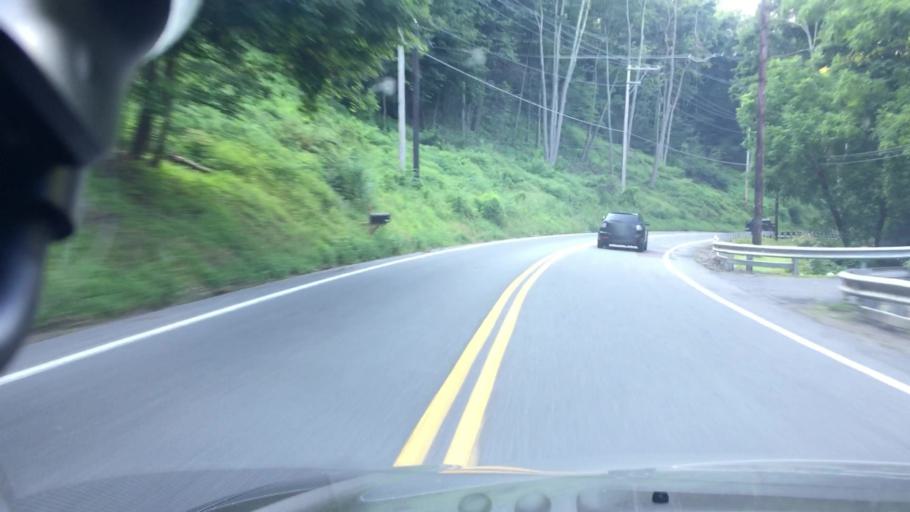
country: US
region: Pennsylvania
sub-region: Columbia County
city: Catawissa
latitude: 40.9350
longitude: -76.4573
